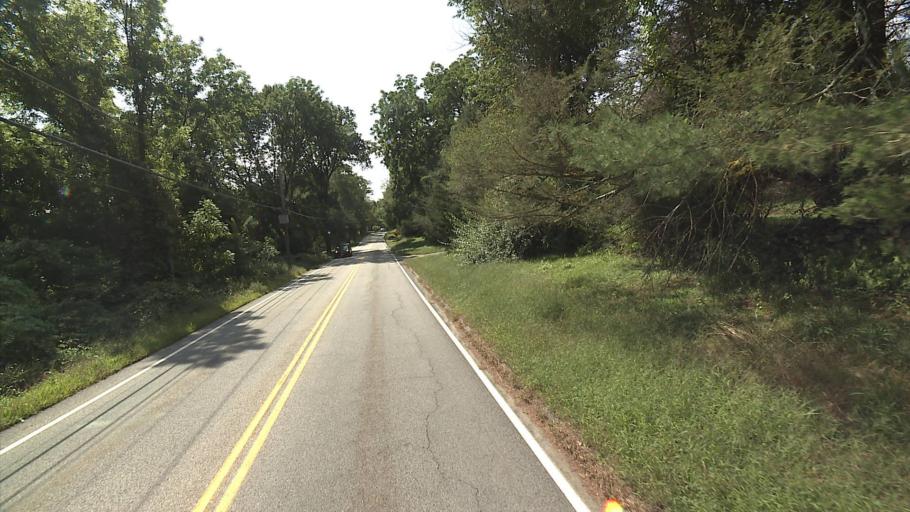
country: US
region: Connecticut
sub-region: Windham County
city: Plainfield Village
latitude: 41.7033
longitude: -71.9682
